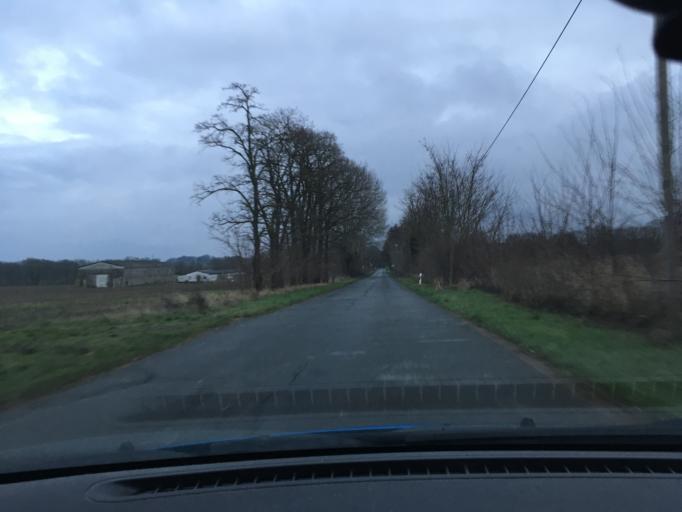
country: DE
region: Mecklenburg-Vorpommern
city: Nostorf
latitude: 53.3912
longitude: 10.6874
